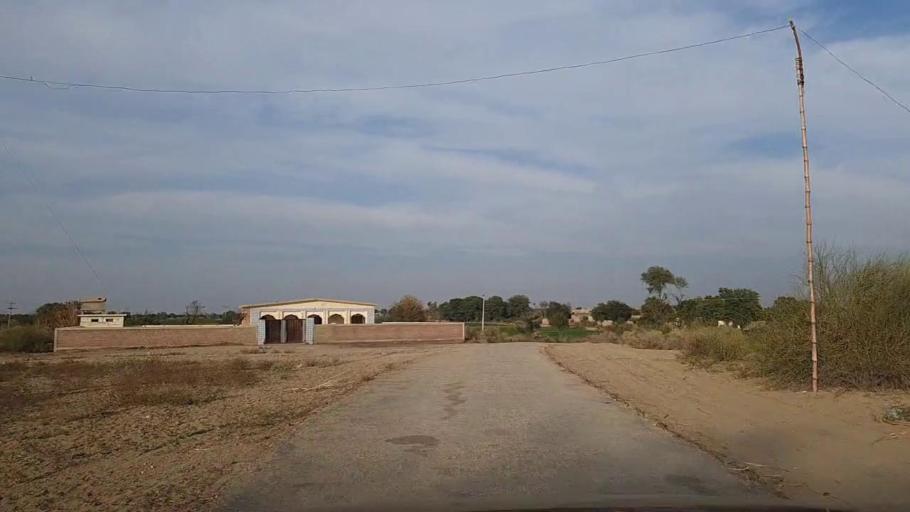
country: PK
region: Sindh
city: Jam Sahib
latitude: 26.4592
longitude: 68.5704
